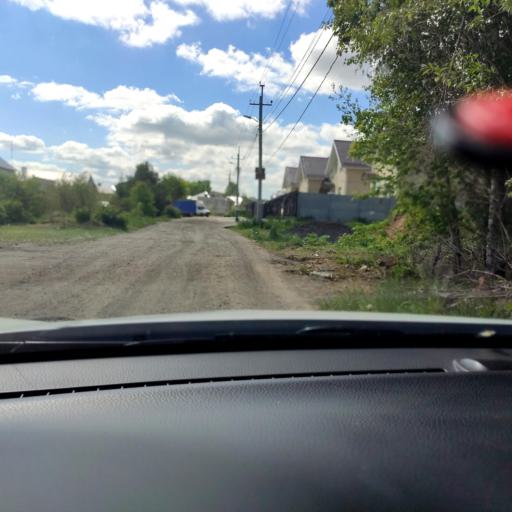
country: RU
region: Tatarstan
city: Stolbishchi
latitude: 55.7524
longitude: 49.2566
